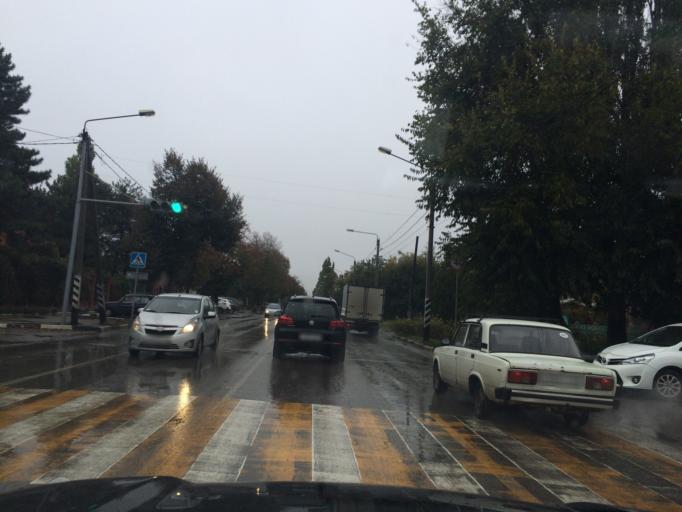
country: RU
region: Rostov
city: Azov
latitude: 47.0946
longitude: 39.4480
